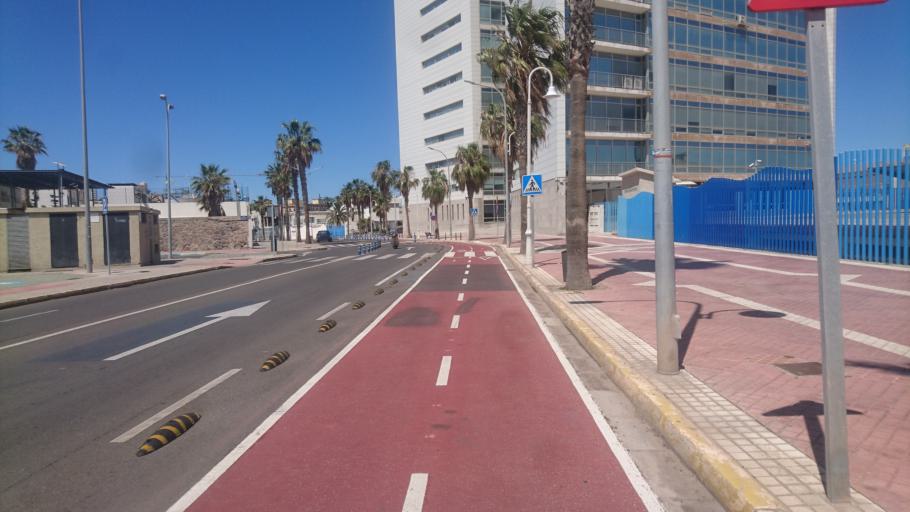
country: ES
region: Melilla
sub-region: Melilla
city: Melilla
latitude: 35.2892
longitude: -2.9366
